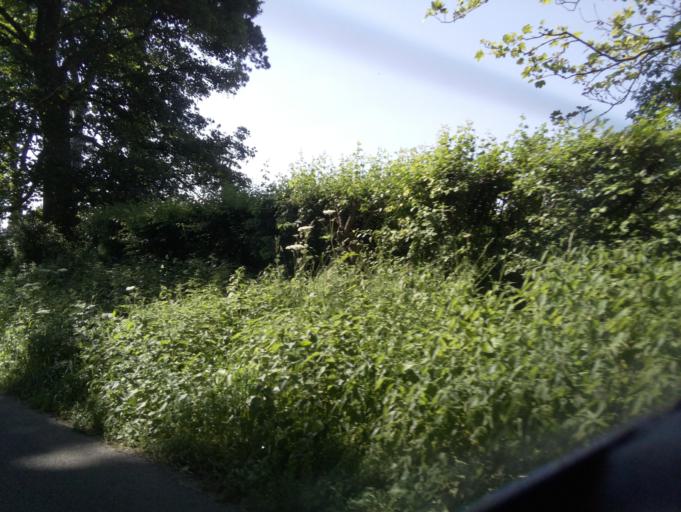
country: GB
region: England
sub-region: Hampshire
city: Andover
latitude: 51.2215
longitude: -1.5204
